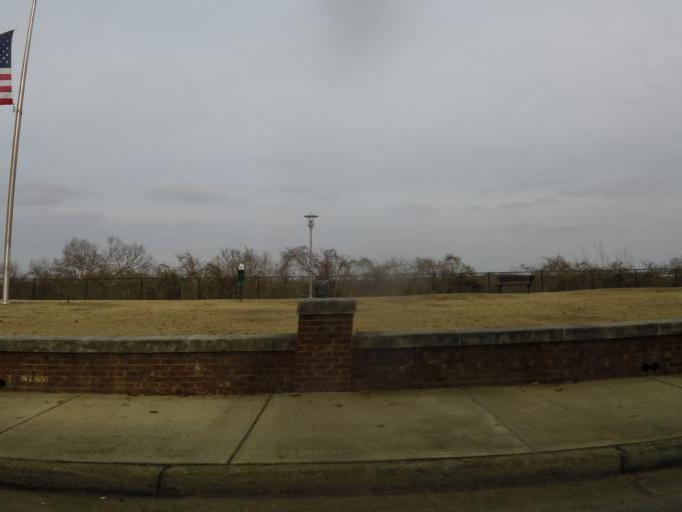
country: US
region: Alabama
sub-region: Montgomery County
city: Montgomery
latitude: 32.3777
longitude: -86.3188
